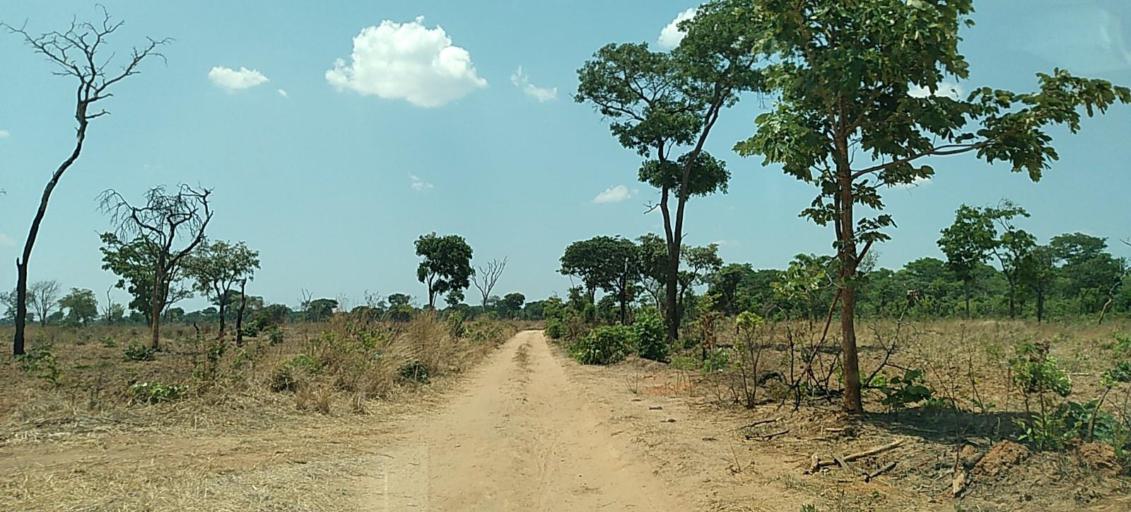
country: ZM
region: Central
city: Kapiri Mposhi
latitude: -13.6589
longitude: 28.4908
